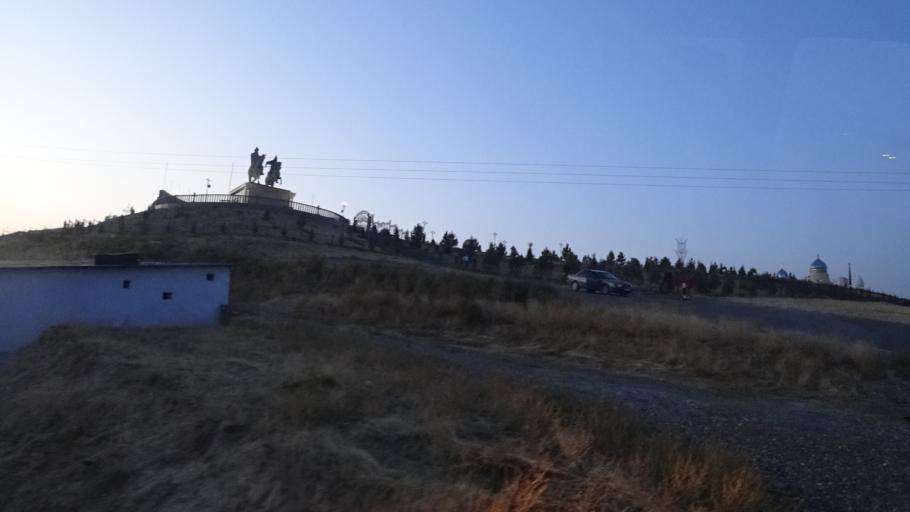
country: KZ
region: Ongtustik Qazaqstan
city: Qazyqurt
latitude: 41.8746
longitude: 69.4279
